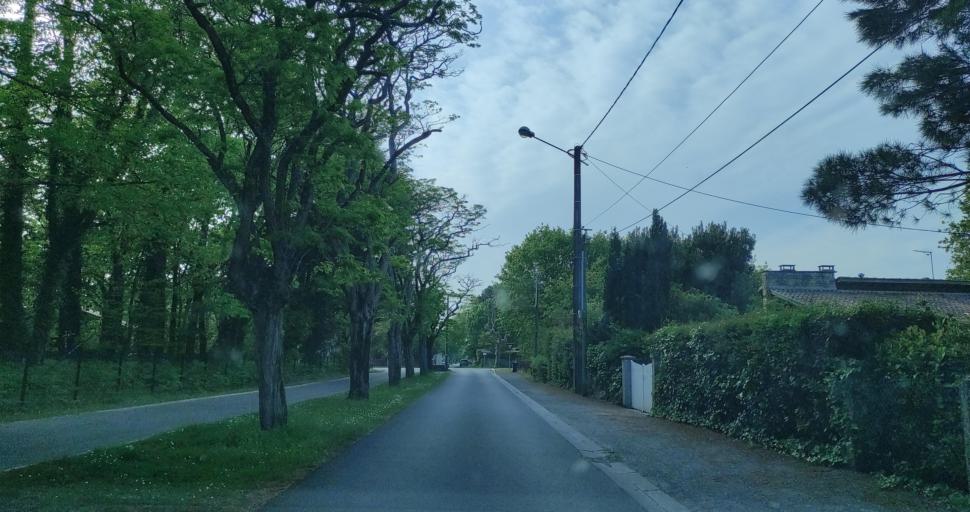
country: FR
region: Aquitaine
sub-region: Departement de la Gironde
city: Ares
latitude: 44.7564
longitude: -1.1324
